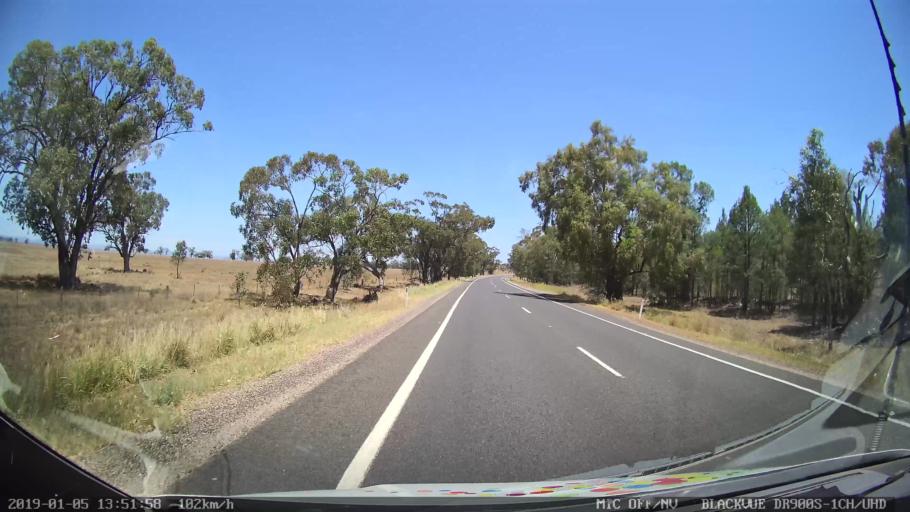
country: AU
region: New South Wales
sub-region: Gunnedah
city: Gunnedah
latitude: -31.0527
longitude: 150.2778
